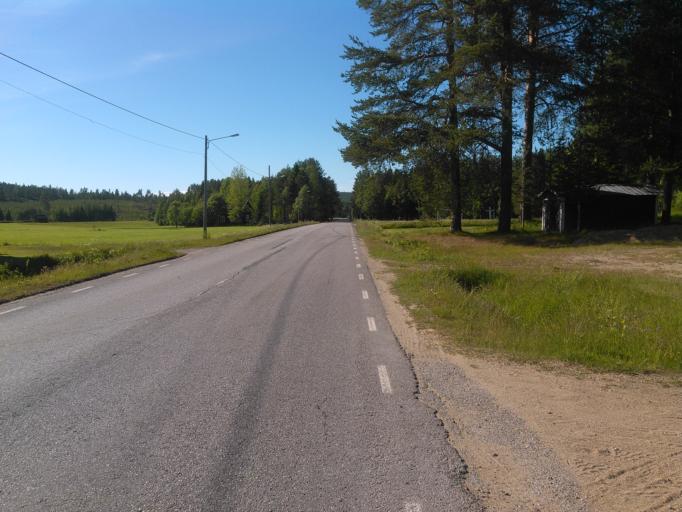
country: SE
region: Vaesterbotten
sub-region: Umea Kommun
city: Roback
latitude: 63.8296
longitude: 20.1143
